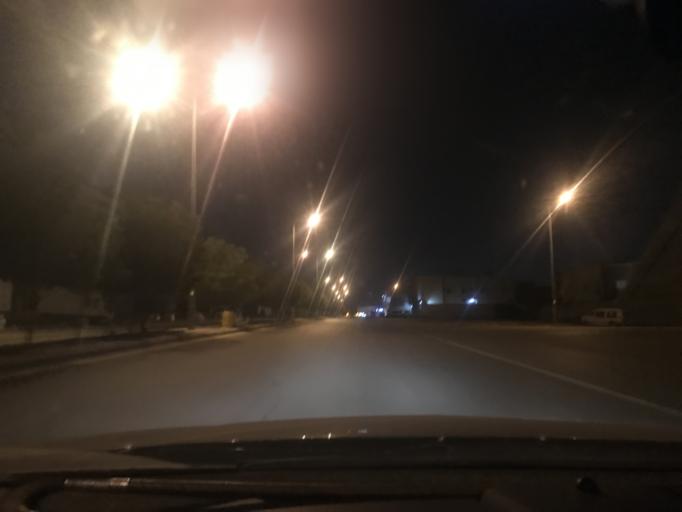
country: SA
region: Ar Riyad
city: Riyadh
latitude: 24.7491
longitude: 46.7538
